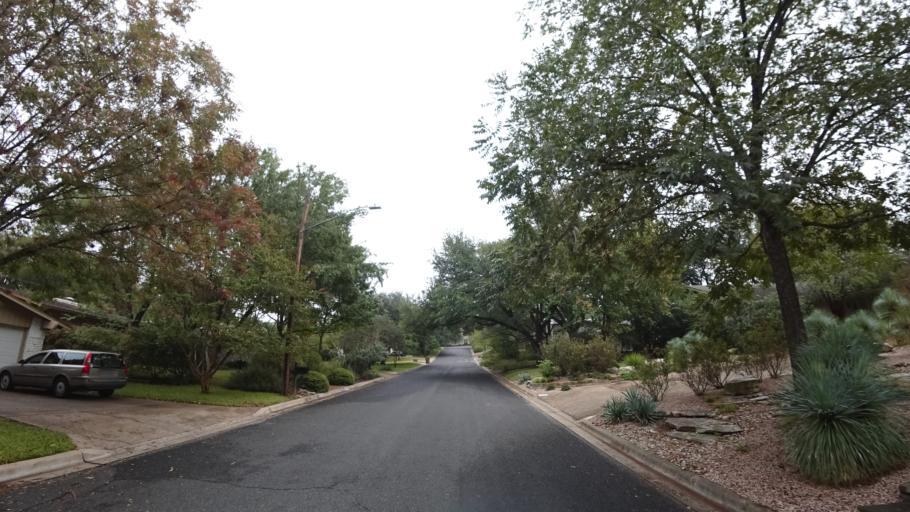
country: US
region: Texas
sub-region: Travis County
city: Rollingwood
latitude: 30.2596
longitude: -97.7774
